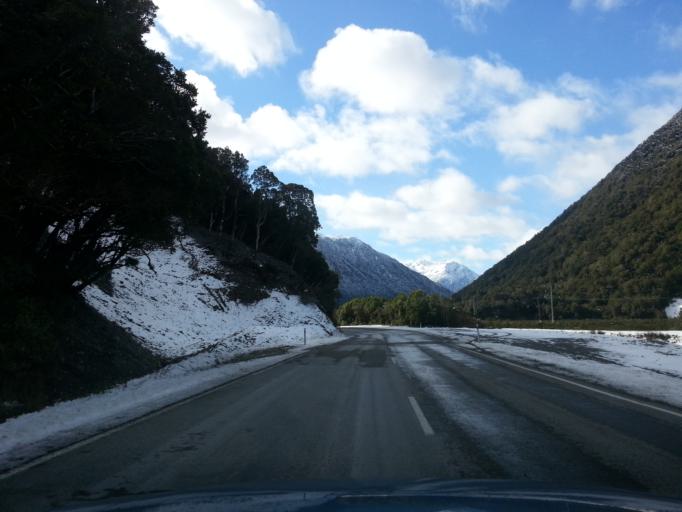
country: NZ
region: West Coast
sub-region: Grey District
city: Greymouth
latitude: -42.8234
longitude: 171.5627
